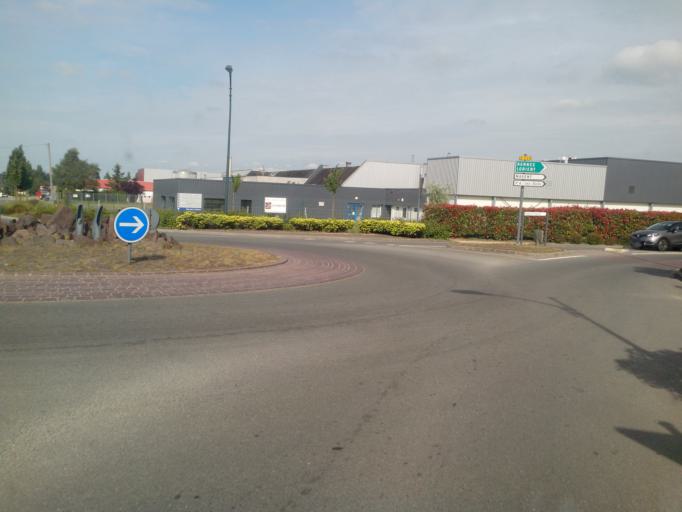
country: FR
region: Brittany
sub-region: Departement d'Ille-et-Vilaine
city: Plelan-le-Grand
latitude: 48.0060
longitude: -2.0881
